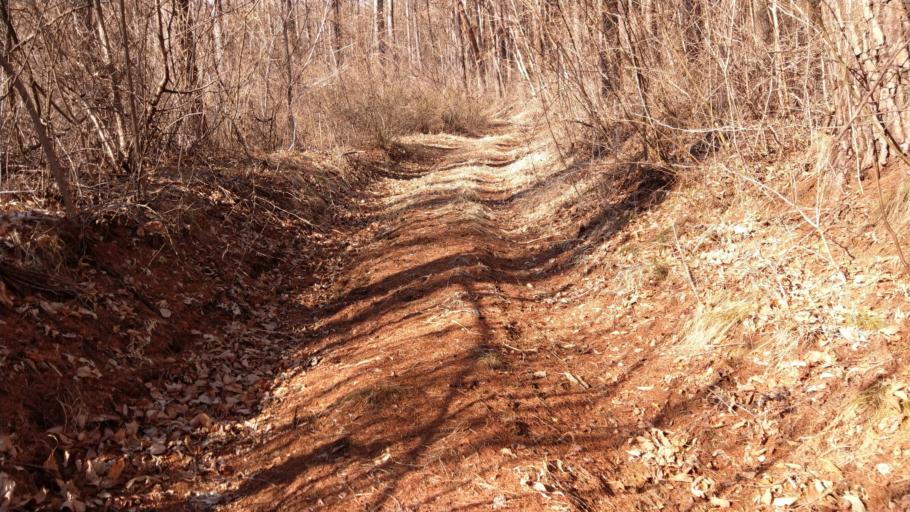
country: JP
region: Nagano
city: Komoro
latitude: 36.3672
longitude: 138.4312
